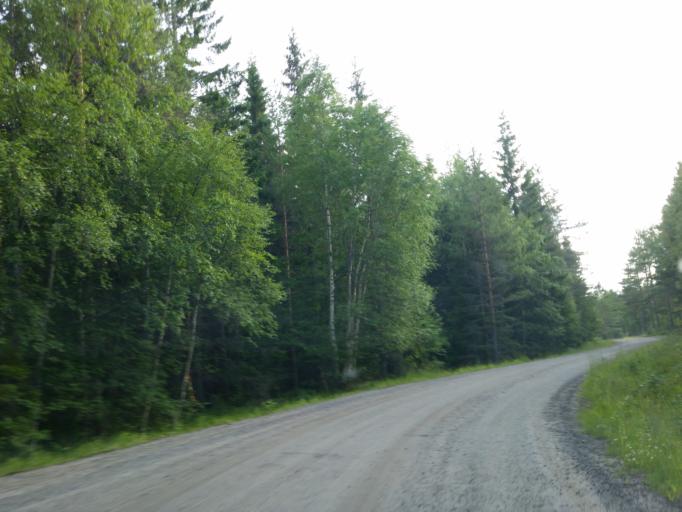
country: SE
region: Vaesterbotten
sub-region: Robertsfors Kommun
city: Robertsfors
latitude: 64.0447
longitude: 20.8507
